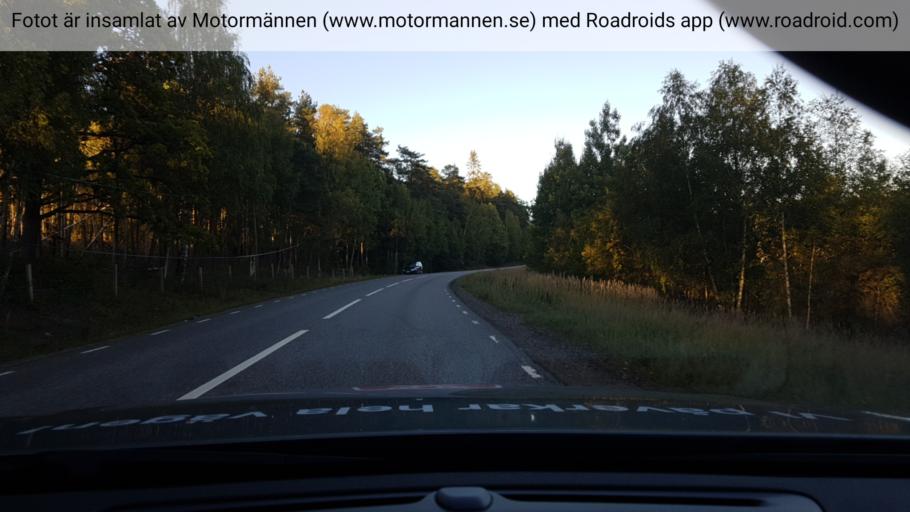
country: SE
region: Stockholm
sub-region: Haninge Kommun
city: Handen
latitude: 59.1884
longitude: 18.1023
